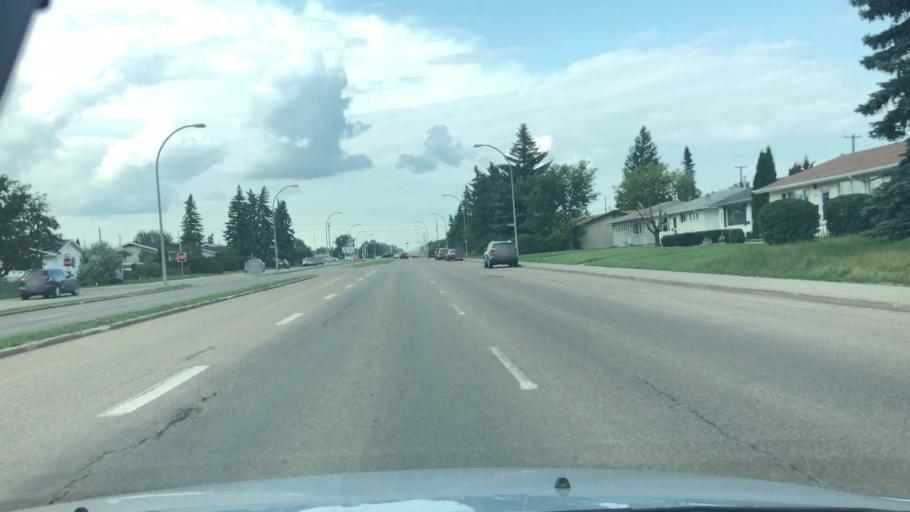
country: CA
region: Alberta
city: Edmonton
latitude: 53.5964
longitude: -113.5167
